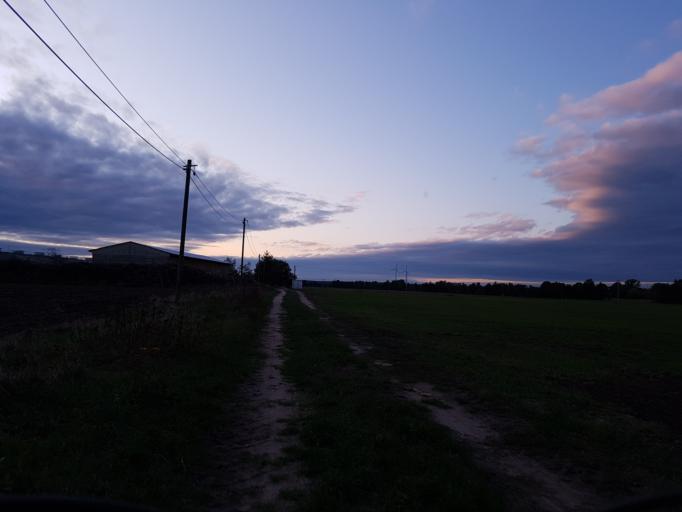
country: DE
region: Brandenburg
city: Schilda
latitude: 51.6104
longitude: 13.3593
